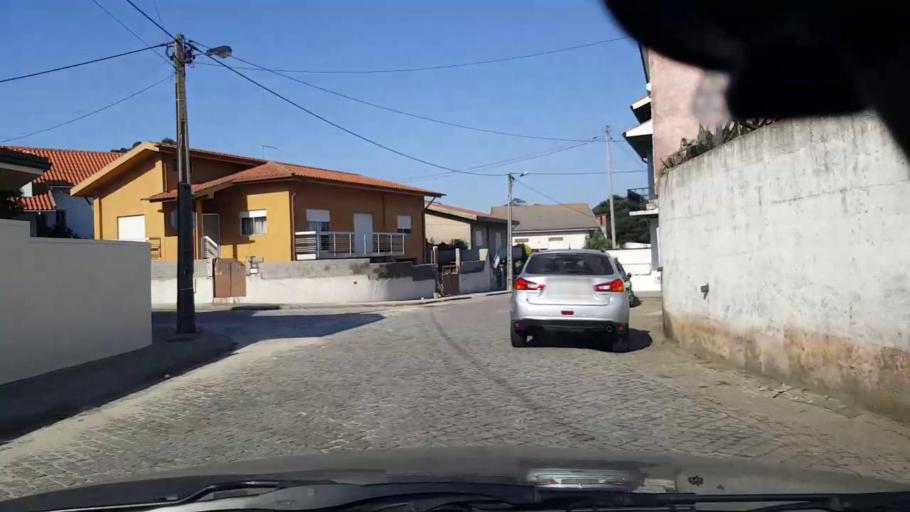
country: PT
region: Porto
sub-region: Vila do Conde
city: Arvore
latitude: 41.3445
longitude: -8.7295
